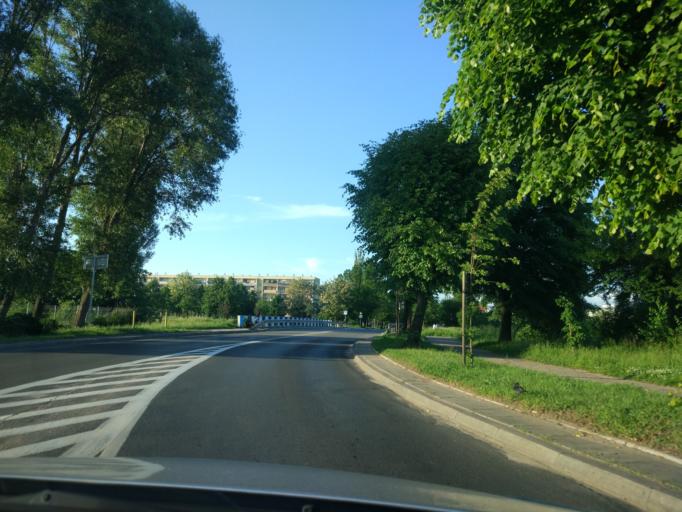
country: PL
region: Lodz Voivodeship
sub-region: Powiat kutnowski
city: Kutno
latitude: 52.2243
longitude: 19.3630
